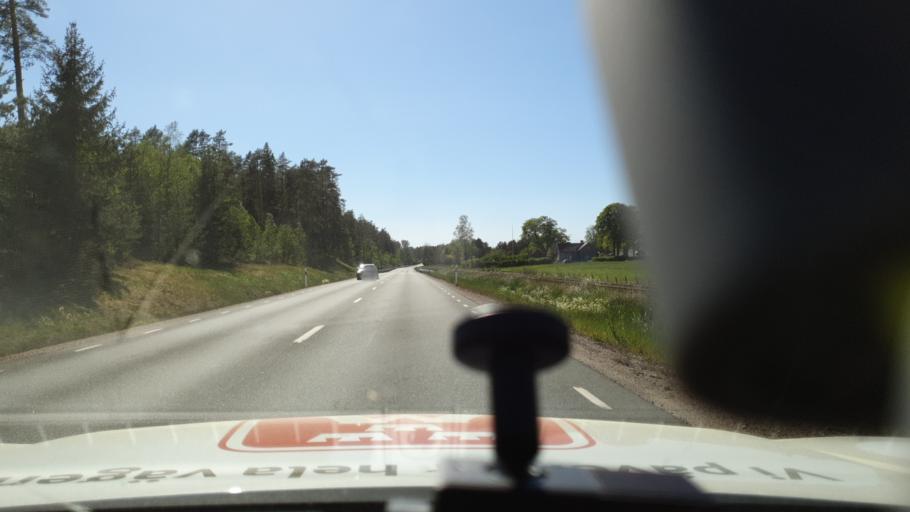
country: SE
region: Kalmar
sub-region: Hultsfreds Kommun
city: Virserum
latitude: 57.3993
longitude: 15.4100
